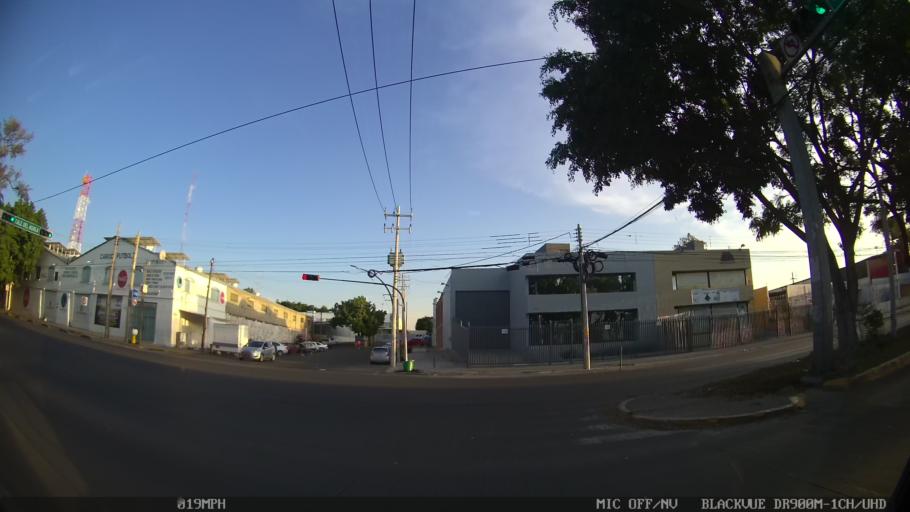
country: MX
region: Jalisco
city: Guadalajara
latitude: 20.6577
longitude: -103.3532
